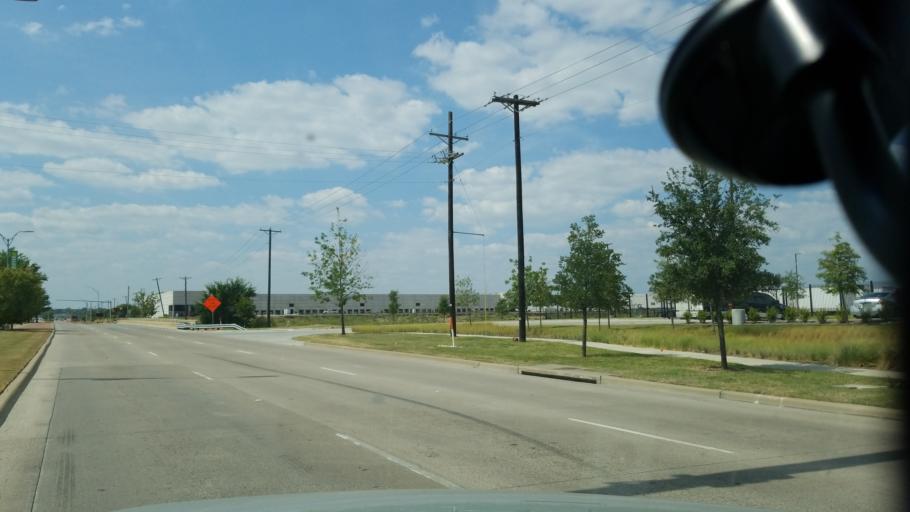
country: US
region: Texas
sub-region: Dallas County
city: Grand Prairie
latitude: 32.7699
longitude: -96.9950
